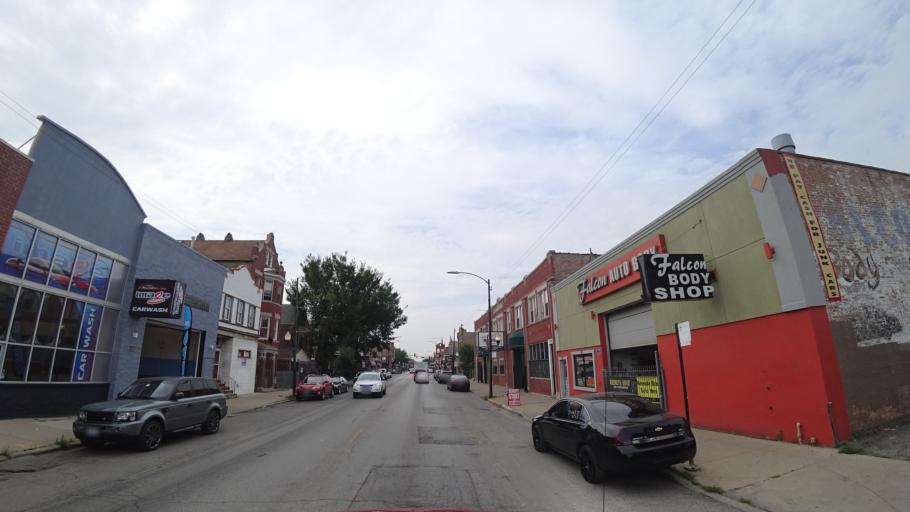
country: US
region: Illinois
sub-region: Cook County
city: Cicero
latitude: 41.8475
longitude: -87.7052
